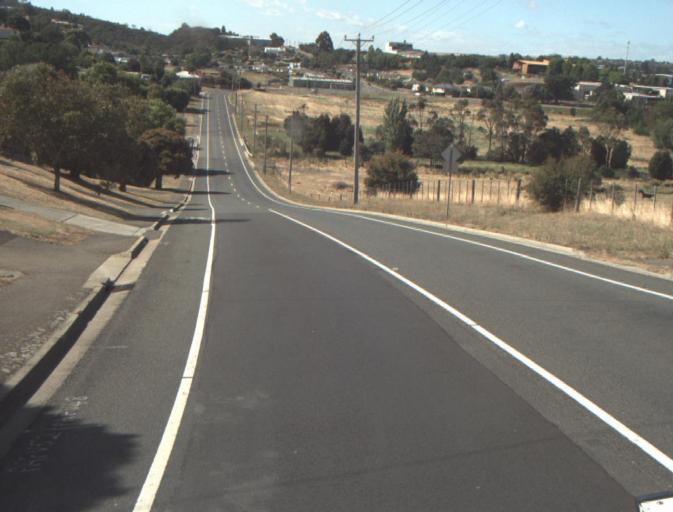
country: AU
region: Tasmania
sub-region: Launceston
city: Newstead
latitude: -41.4312
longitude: 147.1730
